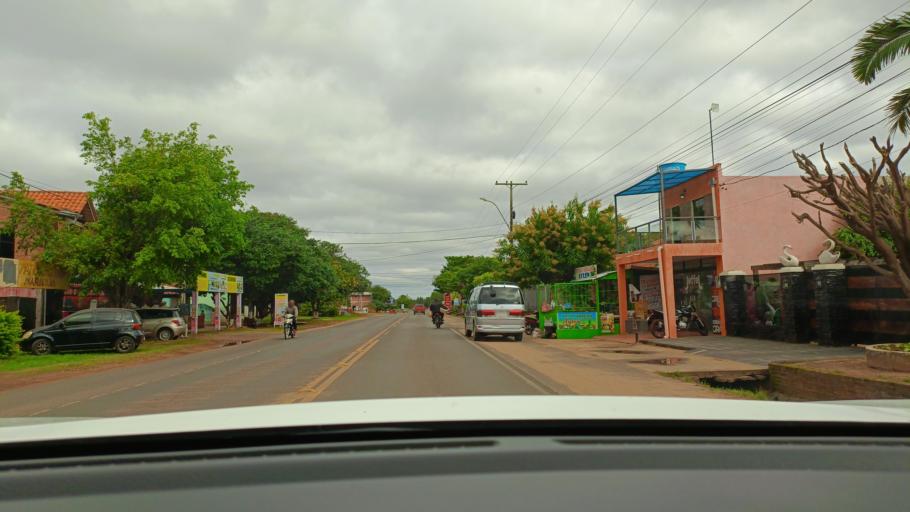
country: PY
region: San Pedro
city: Guayaybi
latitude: -24.6728
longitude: -56.4526
